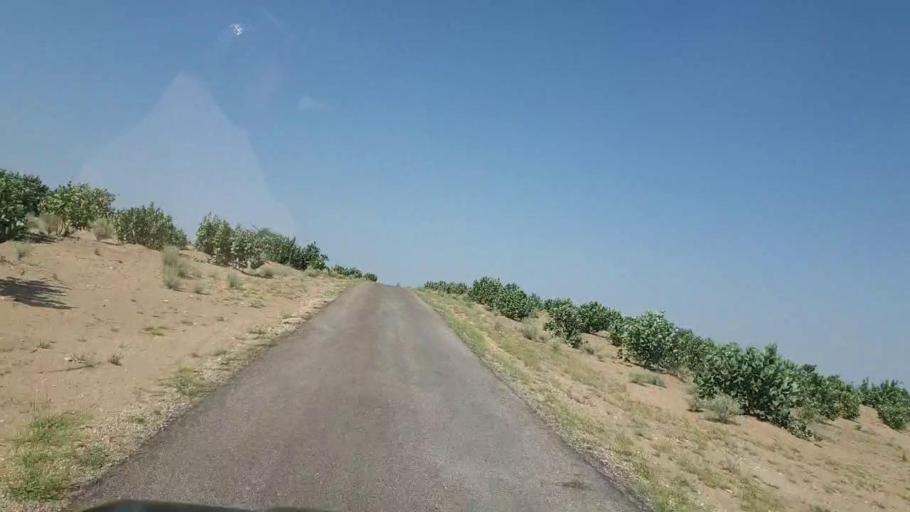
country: PK
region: Sindh
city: Chor
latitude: 25.6373
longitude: 70.3182
